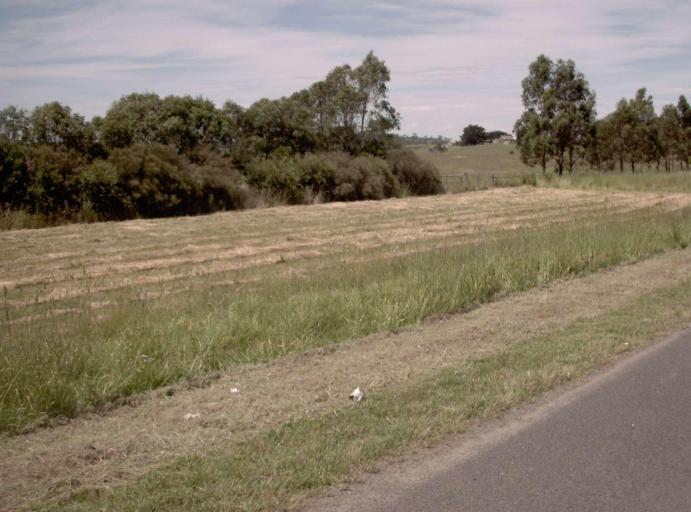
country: AU
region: Victoria
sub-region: Latrobe
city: Traralgon
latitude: -38.1583
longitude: 146.7190
